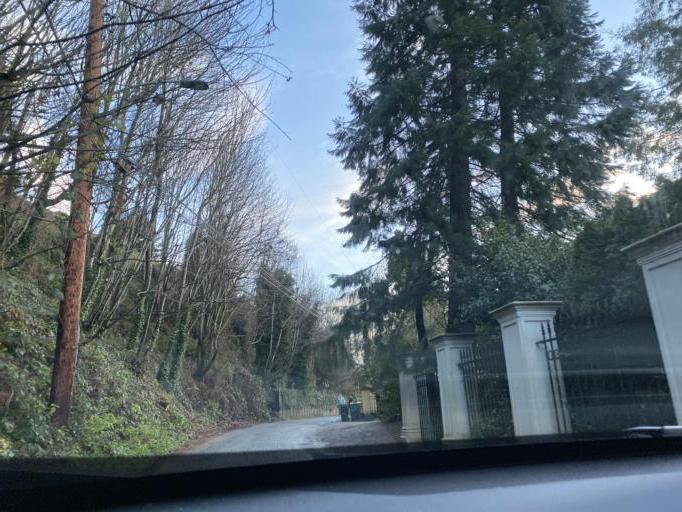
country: US
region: Washington
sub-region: King County
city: Seattle
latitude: 47.6477
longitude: -122.4161
